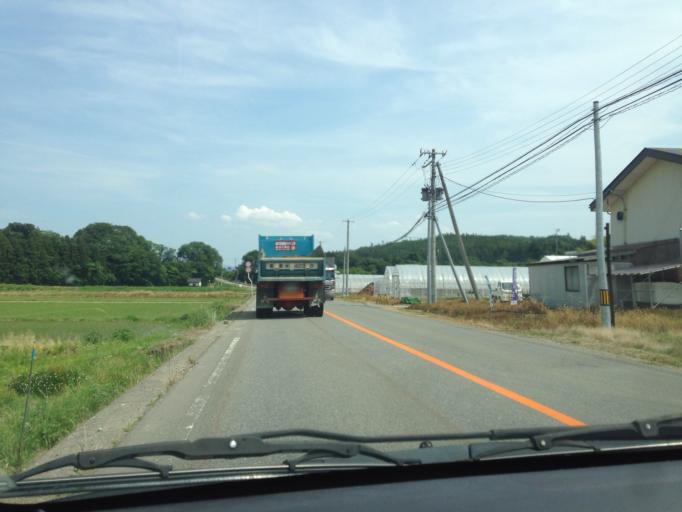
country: JP
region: Fukushima
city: Kitakata
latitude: 37.6091
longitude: 139.8025
